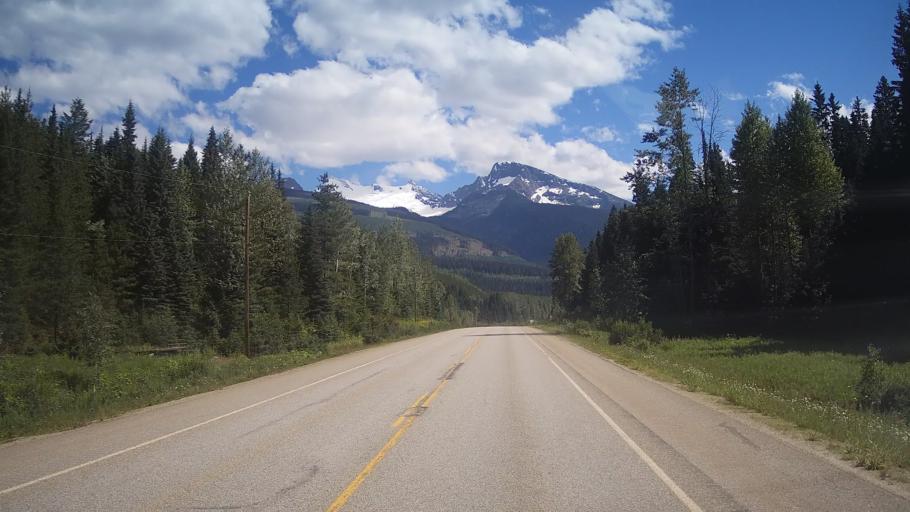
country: CA
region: Alberta
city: Jasper Park Lodge
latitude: 52.5907
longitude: -119.0989
